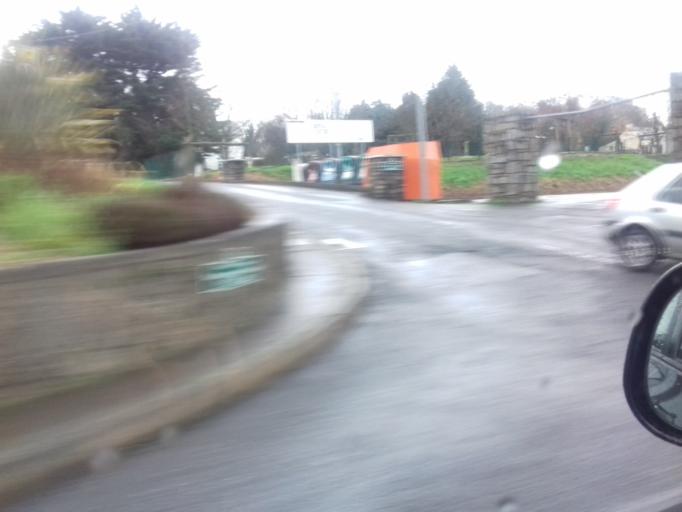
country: IE
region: Leinster
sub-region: Kilkenny
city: Graiguenamanagh
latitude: 52.5433
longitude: -6.9575
